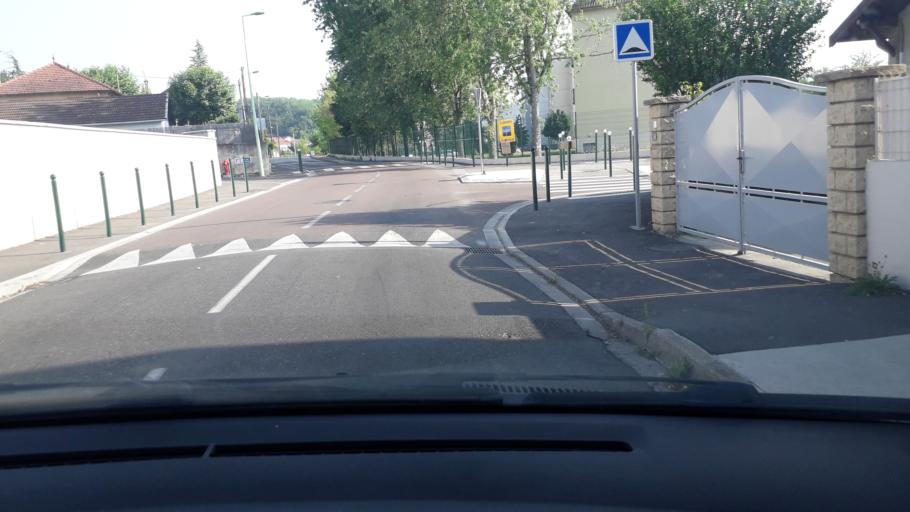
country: FR
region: Rhone-Alpes
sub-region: Departement de l'Isere
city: Pont-de-Cheruy
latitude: 45.7598
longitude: 5.1785
